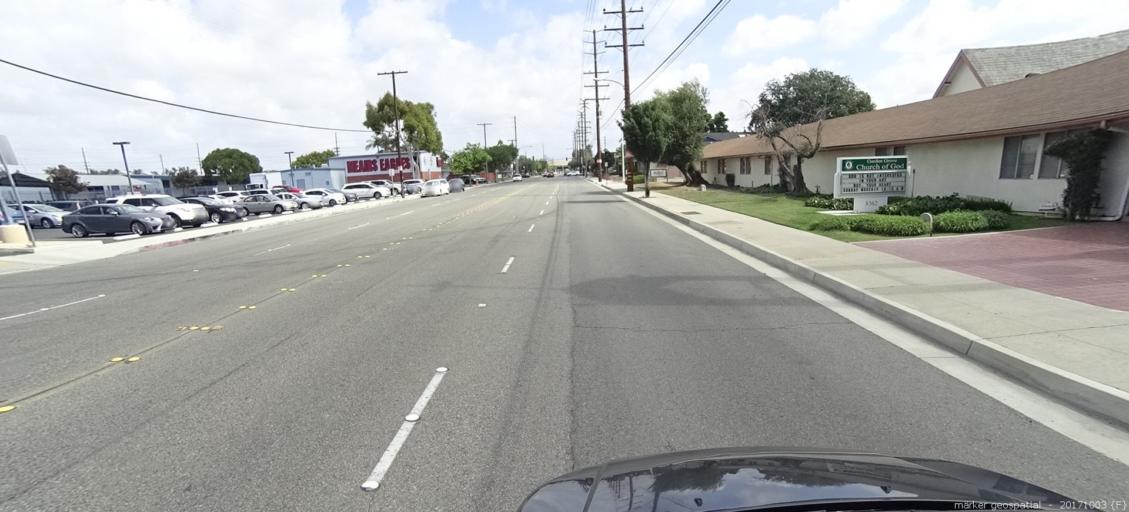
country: US
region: California
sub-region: Orange County
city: Midway City
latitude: 33.7666
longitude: -117.9833
